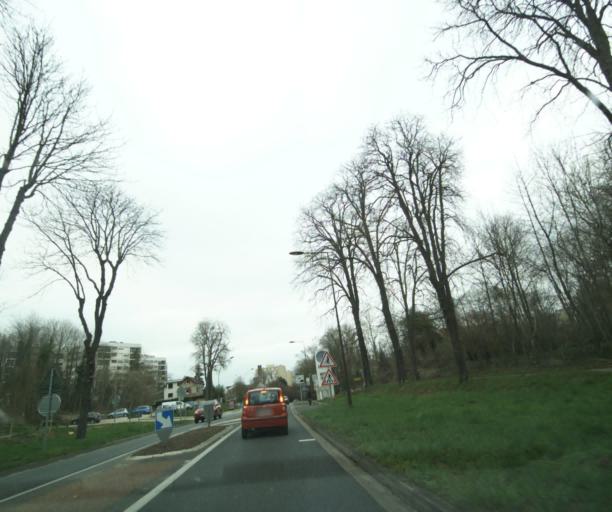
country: FR
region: Ile-de-France
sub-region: Departement des Yvelines
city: Poissy
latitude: 48.9232
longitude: 2.0548
